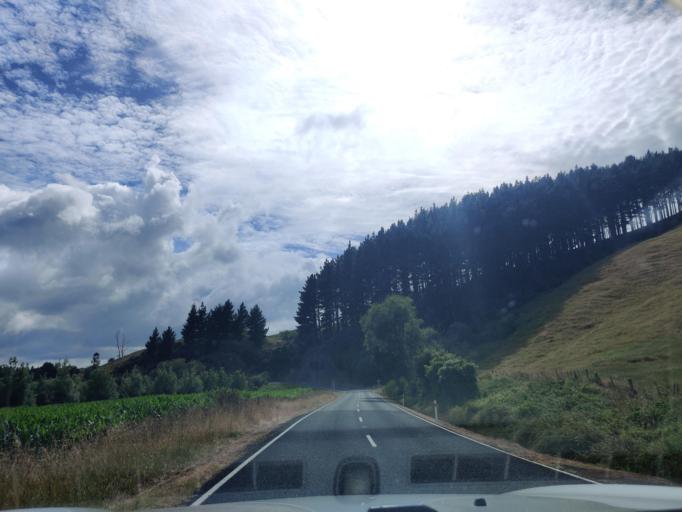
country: NZ
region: Waikato
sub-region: Otorohanga District
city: Otorohanga
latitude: -38.0966
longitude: 175.1418
